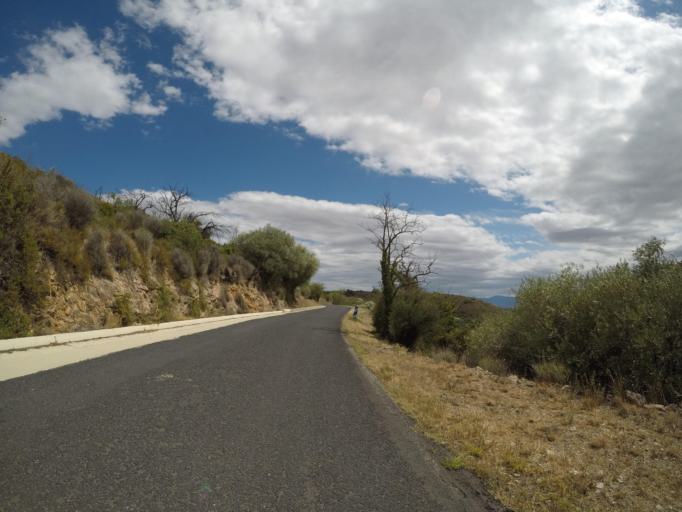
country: FR
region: Languedoc-Roussillon
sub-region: Departement des Pyrenees-Orientales
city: Baixas
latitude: 42.7567
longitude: 2.7649
